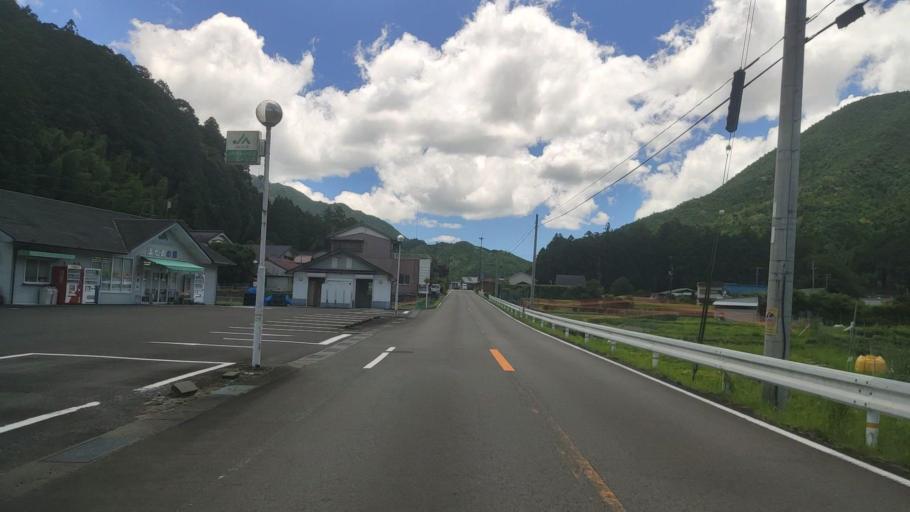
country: JP
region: Mie
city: Owase
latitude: 33.9793
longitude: 136.0512
